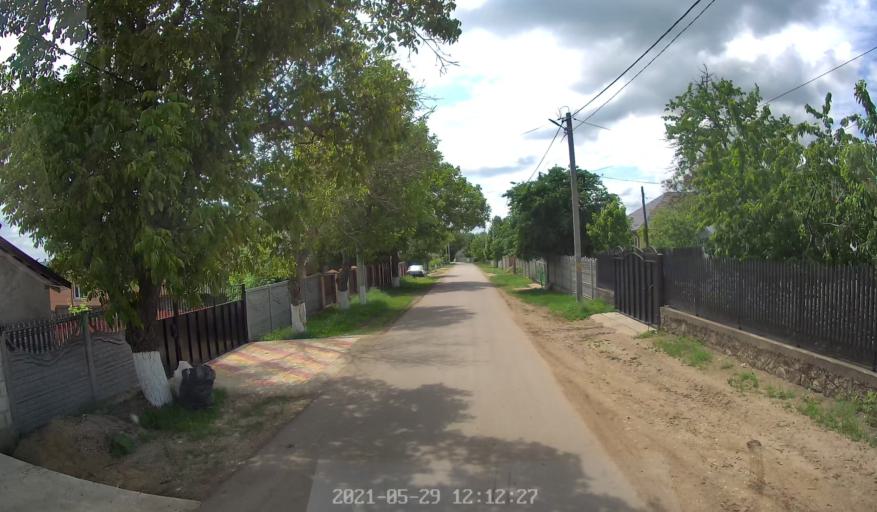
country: MD
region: Hincesti
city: Hincesti
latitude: 46.8793
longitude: 28.6318
